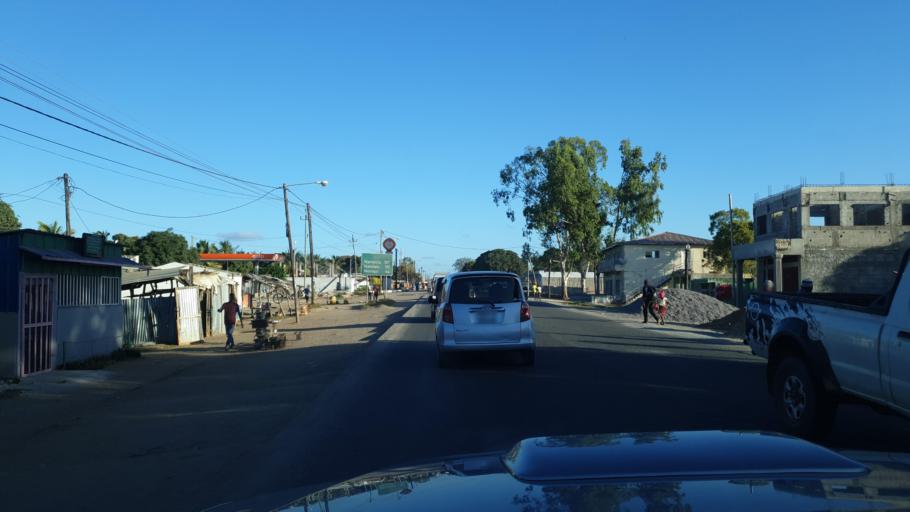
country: MZ
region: Nampula
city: Nacala
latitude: -14.5764
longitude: 40.6816
